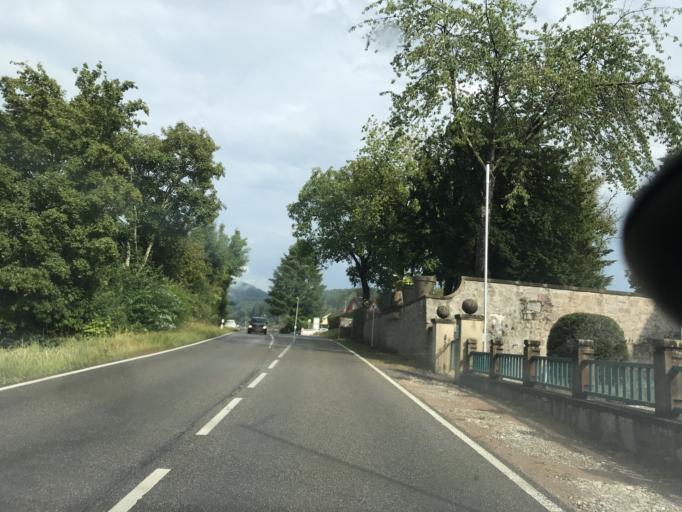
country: DE
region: Baden-Wuerttemberg
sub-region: Freiburg Region
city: Kandern
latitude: 47.7152
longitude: 7.6501
